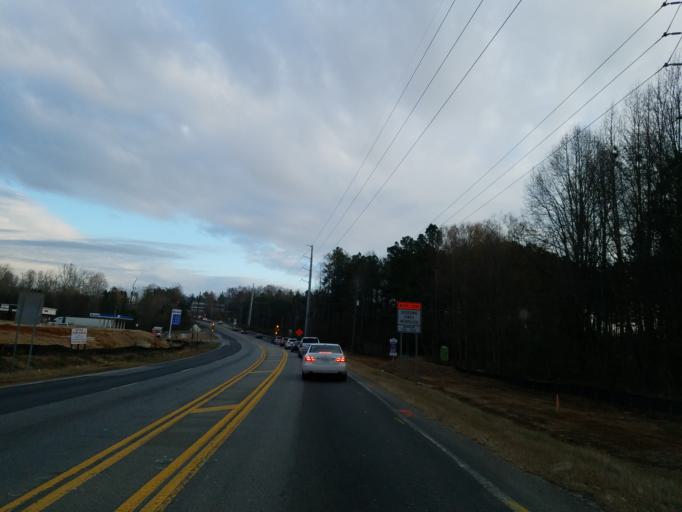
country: US
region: Georgia
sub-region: Forsyth County
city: Cumming
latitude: 34.2657
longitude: -84.0908
